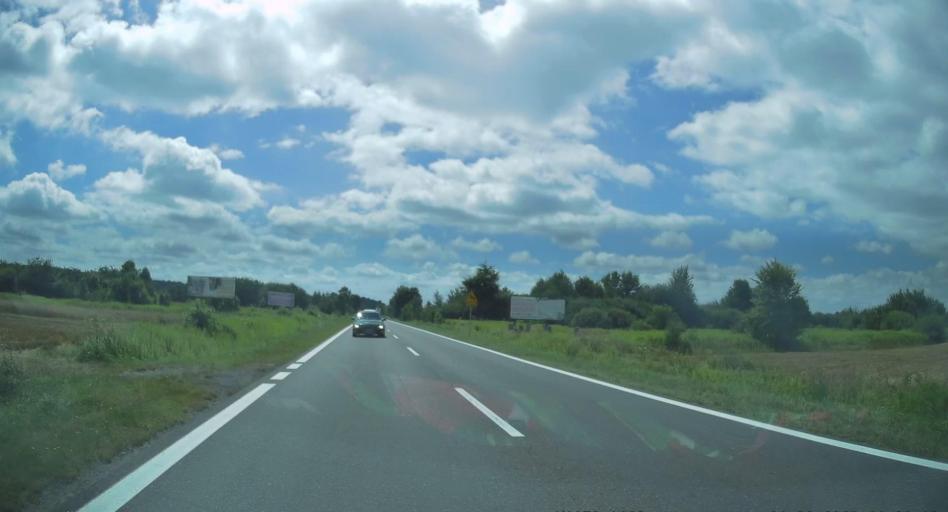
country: PL
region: Subcarpathian Voivodeship
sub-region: Powiat tarnobrzeski
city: Baranow Sandomierski
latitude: 50.4996
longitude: 21.5710
